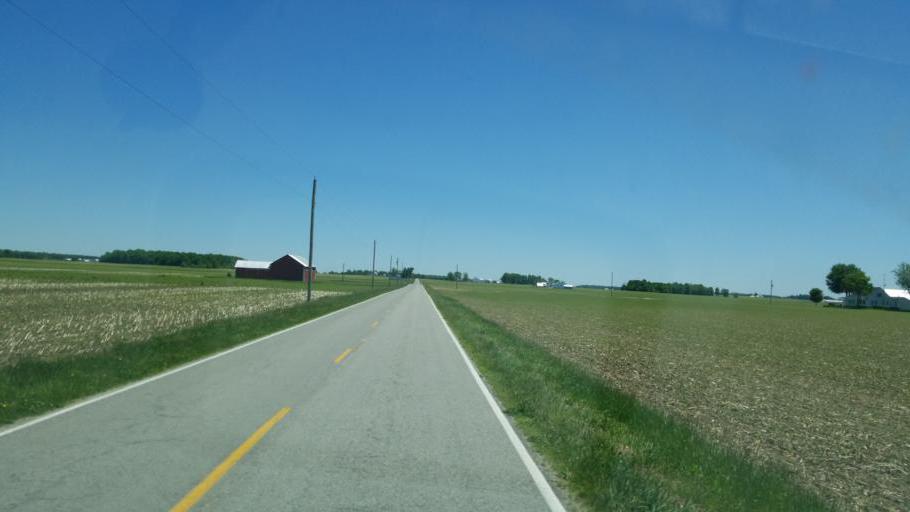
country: US
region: Ohio
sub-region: Darke County
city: Union City
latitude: 40.2814
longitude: -84.7464
